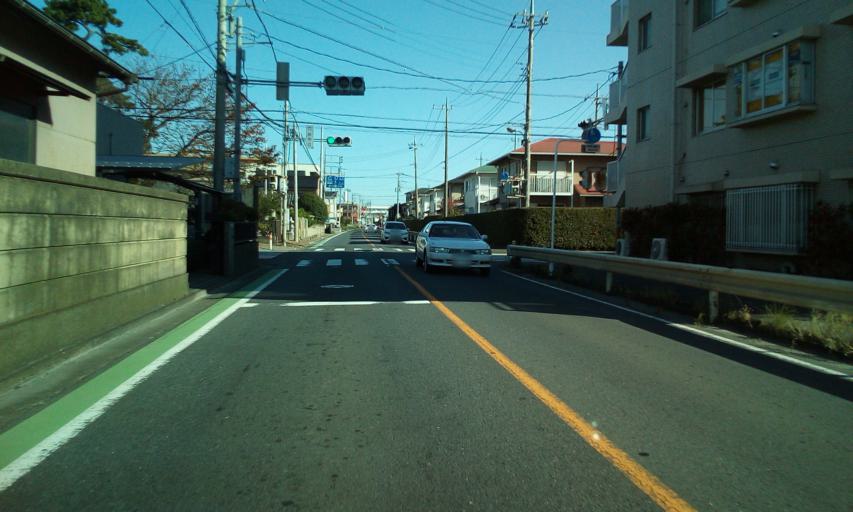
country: JP
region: Chiba
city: Nagareyama
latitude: 35.8576
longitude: 139.8852
